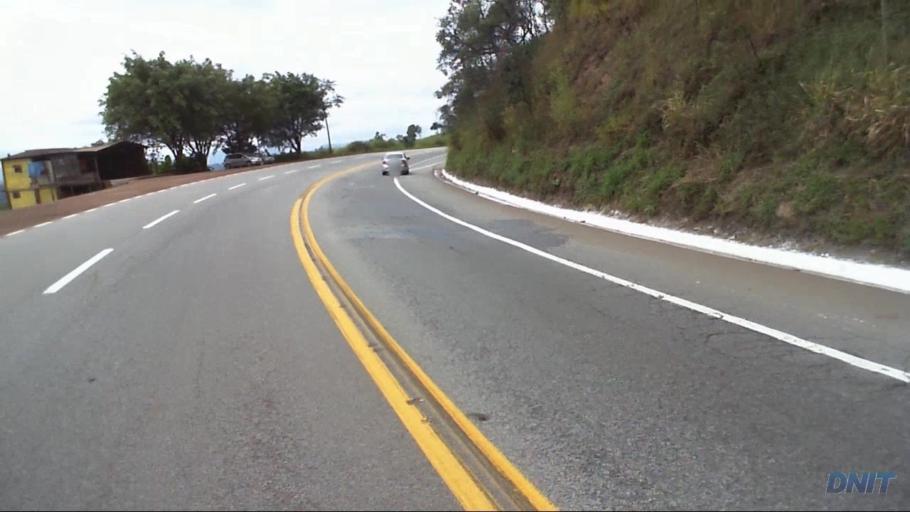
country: BR
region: Minas Gerais
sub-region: Caete
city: Caete
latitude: -19.7869
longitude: -43.6894
